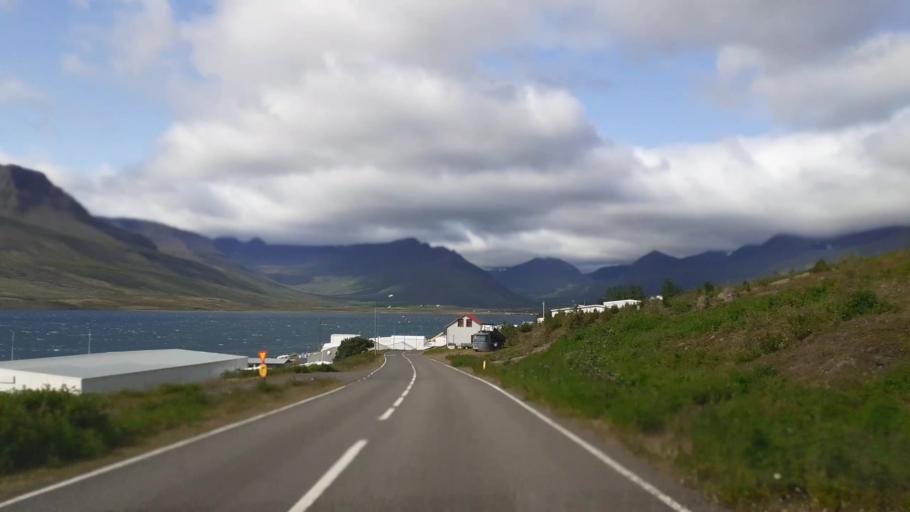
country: IS
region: East
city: Eskifjoerdur
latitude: 64.9248
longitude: -13.9907
